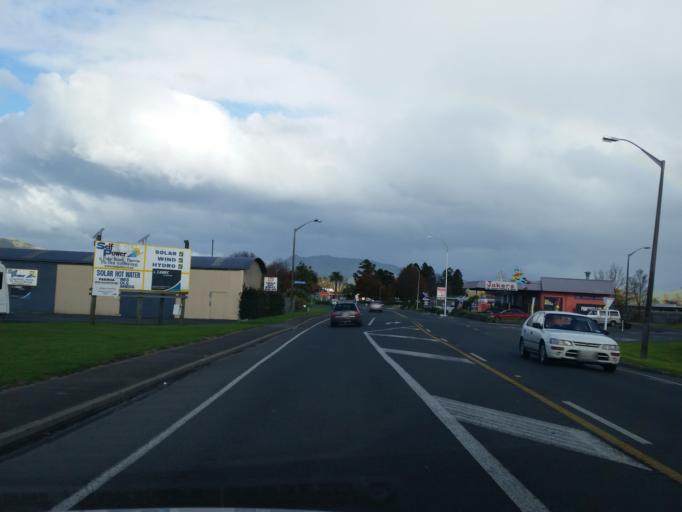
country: NZ
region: Waikato
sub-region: Hauraki District
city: Paeroa
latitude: -37.3741
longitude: 175.6653
